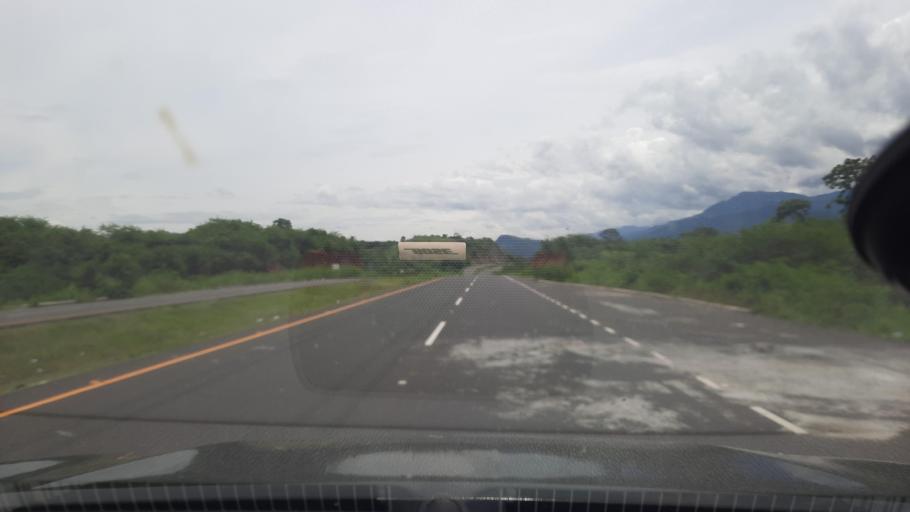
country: HN
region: Valle
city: Aramecina
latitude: 13.7393
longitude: -87.7197
